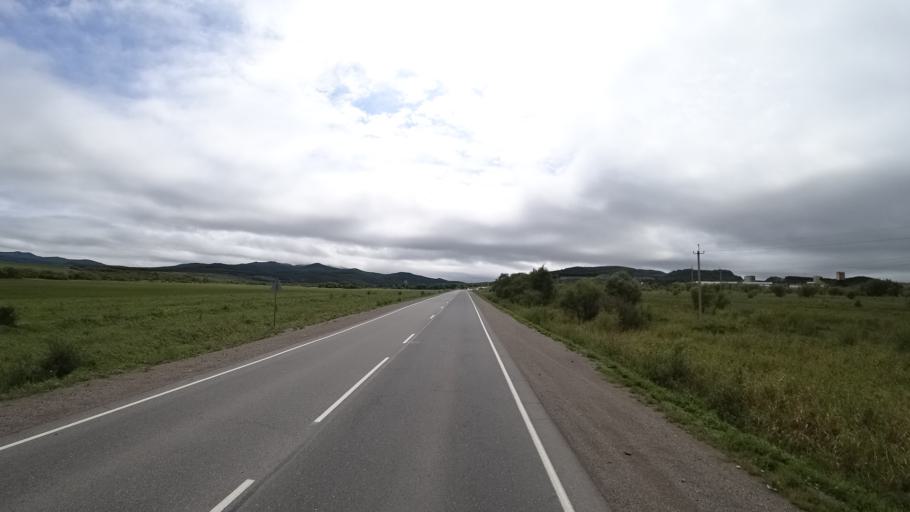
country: RU
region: Primorskiy
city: Monastyrishche
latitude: 44.1746
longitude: 132.4413
